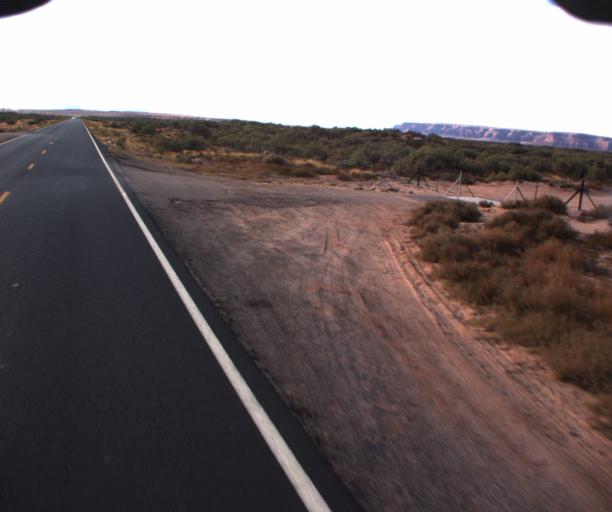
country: US
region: Arizona
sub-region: Apache County
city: Many Farms
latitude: 36.6408
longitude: -109.5886
